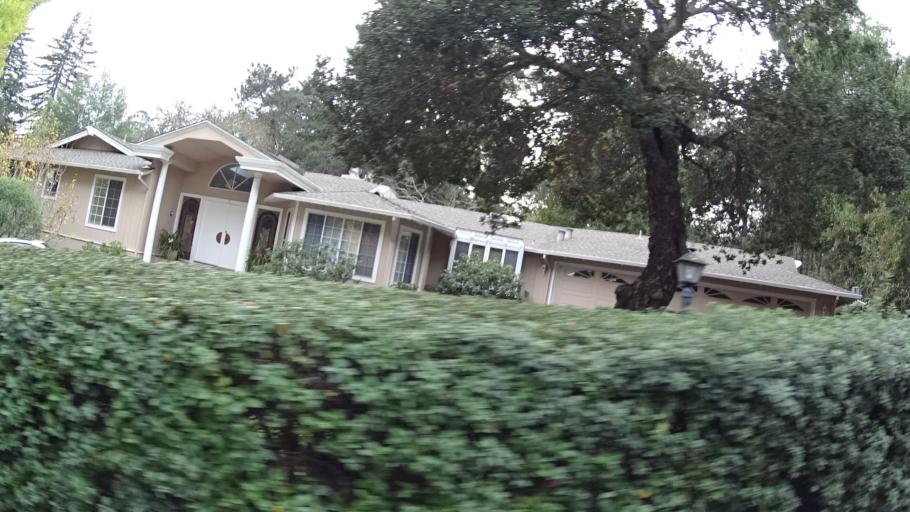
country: US
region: California
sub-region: San Mateo County
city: Hillsborough
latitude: 37.5729
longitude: -122.3719
